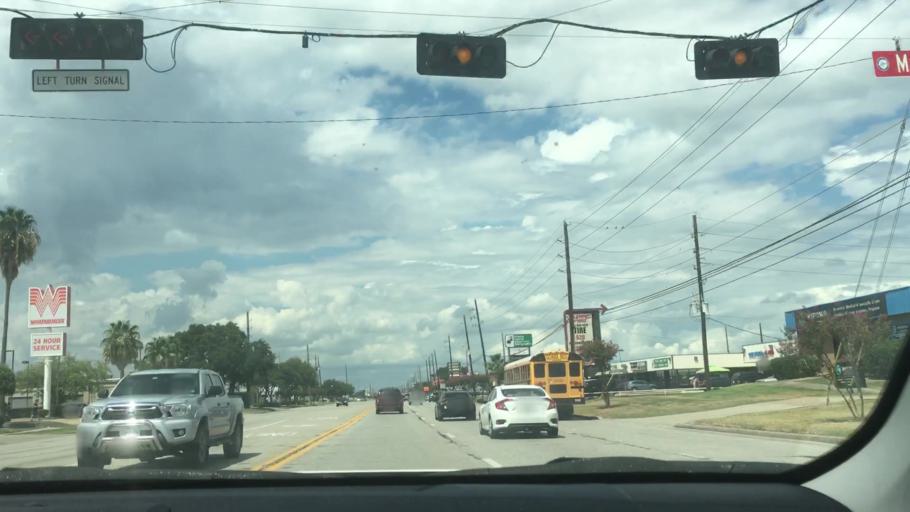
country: US
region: Texas
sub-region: Fort Bend County
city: Stafford
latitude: 29.6327
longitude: -95.5650
